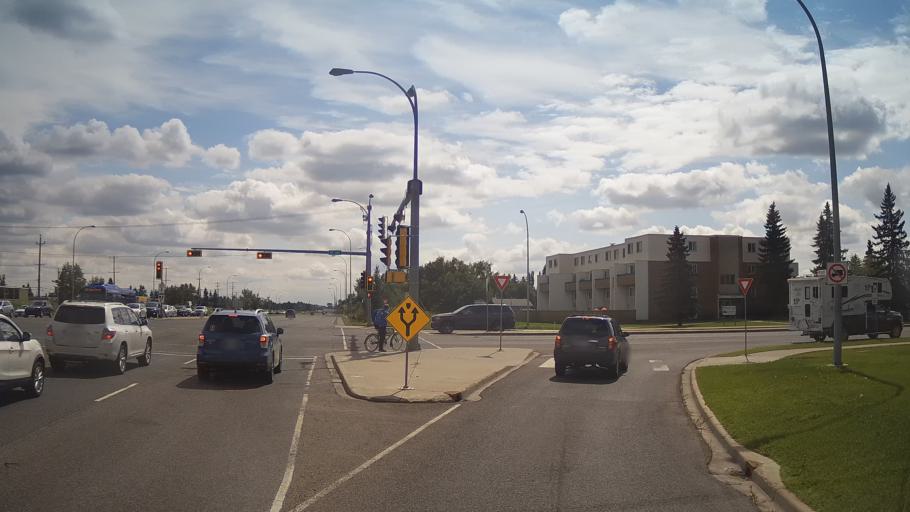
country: CA
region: Alberta
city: St. Albert
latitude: 53.5205
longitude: -113.6157
